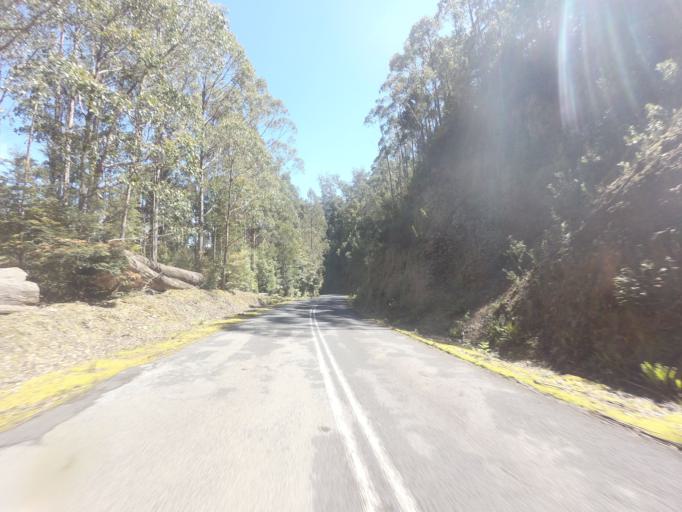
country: AU
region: Tasmania
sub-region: Huon Valley
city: Geeveston
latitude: -42.8201
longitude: 146.3376
